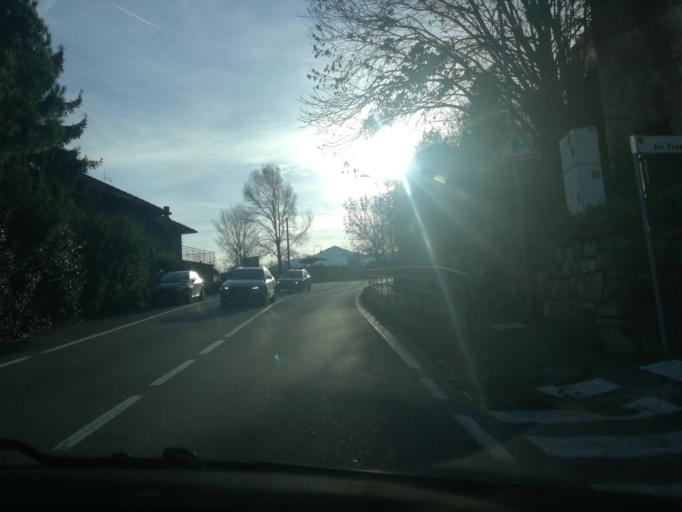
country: IT
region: Lombardy
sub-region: Provincia di Bergamo
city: Lovere
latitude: 45.8090
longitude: 10.0675
